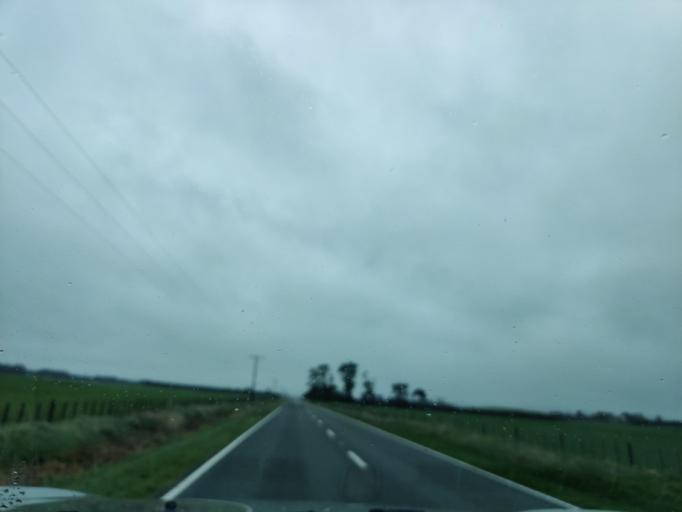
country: NZ
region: Hawke's Bay
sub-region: Hastings District
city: Hastings
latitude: -40.0199
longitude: 176.2814
